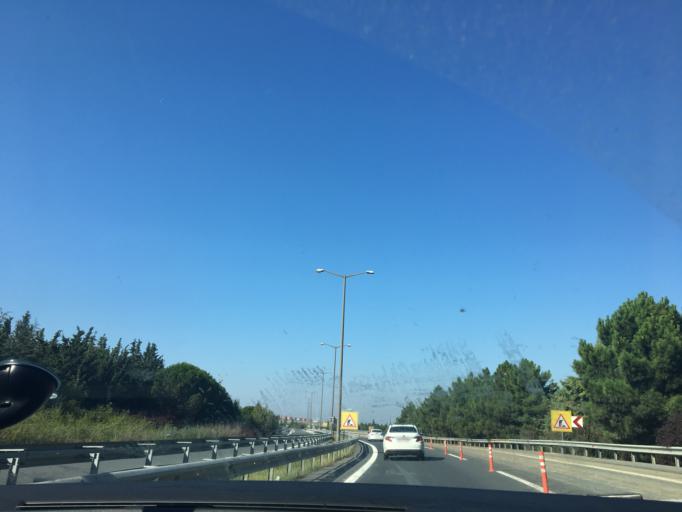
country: TR
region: Istanbul
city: Silivri
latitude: 41.1205
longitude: 28.1863
